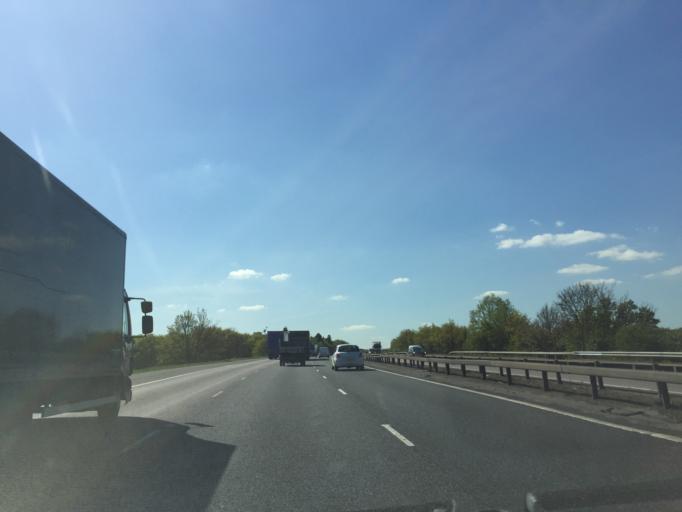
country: GB
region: England
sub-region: Essex
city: Epping
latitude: 51.7116
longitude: 0.1457
